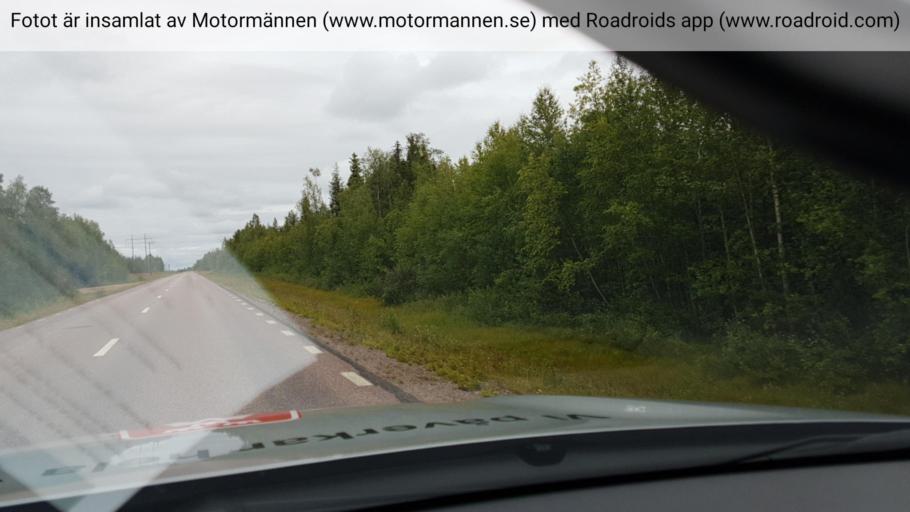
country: SE
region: Norrbotten
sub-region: Pajala Kommun
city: Pajala
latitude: 67.0915
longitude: 22.5661
